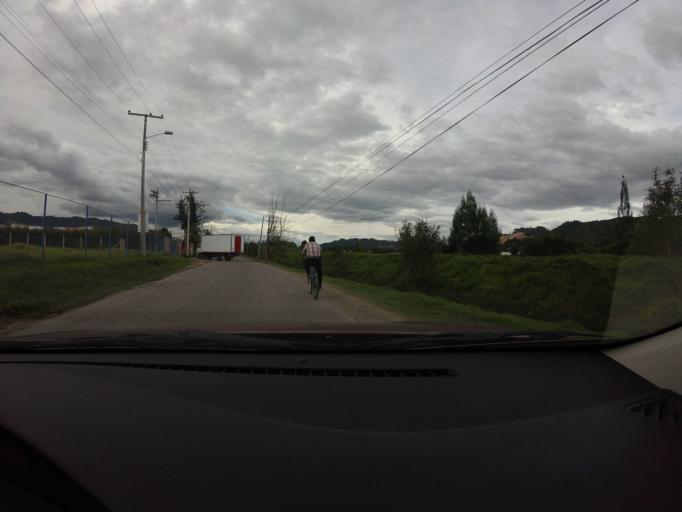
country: CO
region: Cundinamarca
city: Cajica
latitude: 4.9192
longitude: -74.0099
